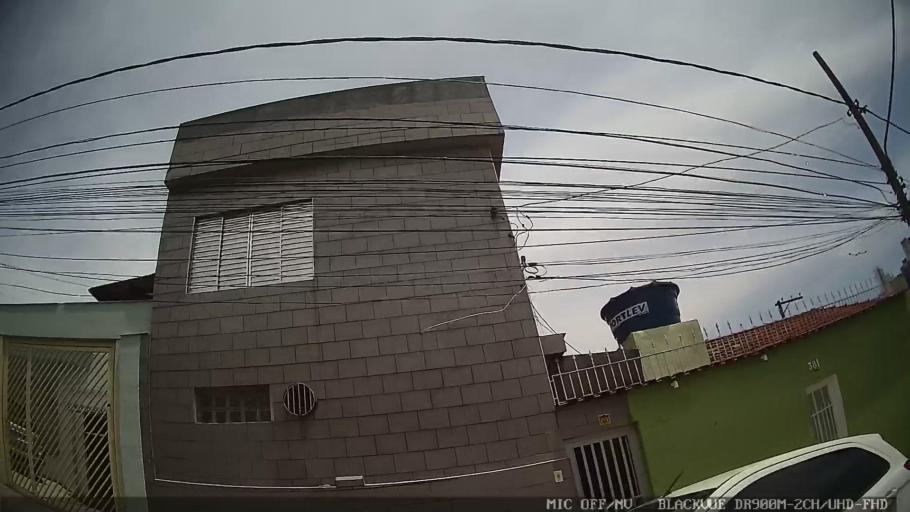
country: BR
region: Sao Paulo
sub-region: Sao Caetano Do Sul
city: Sao Caetano do Sul
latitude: -23.5641
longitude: -46.5641
